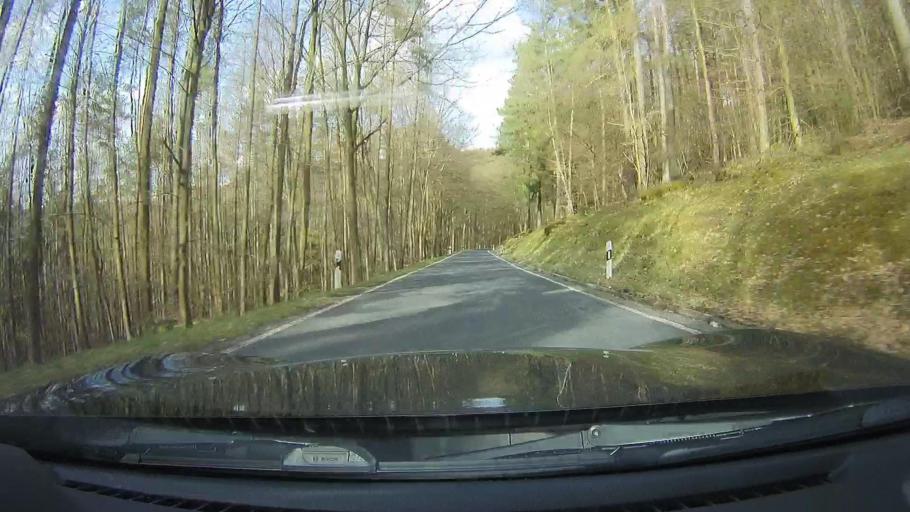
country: DE
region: Bavaria
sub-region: Regierungsbezirk Unterfranken
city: Weilbach
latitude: 49.6227
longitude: 9.2529
